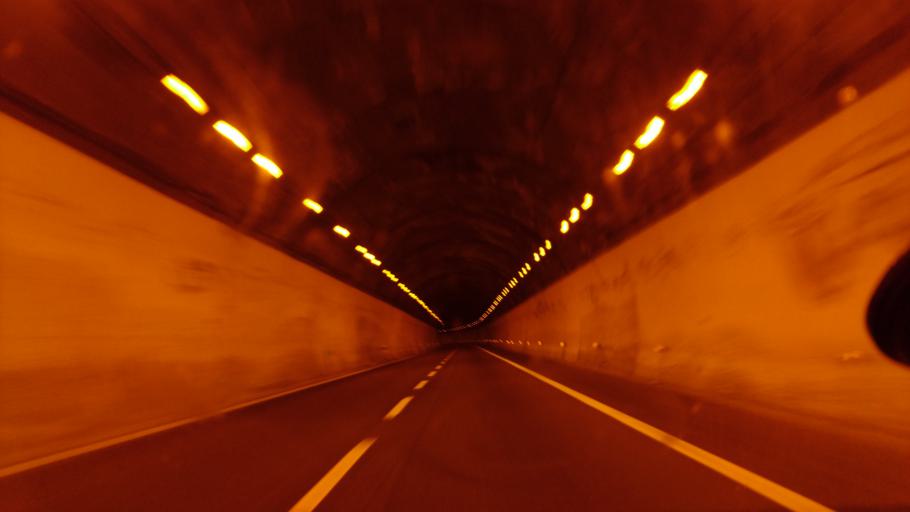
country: IT
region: Liguria
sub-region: Provincia di Savona
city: Altare
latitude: 44.3349
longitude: 8.3725
